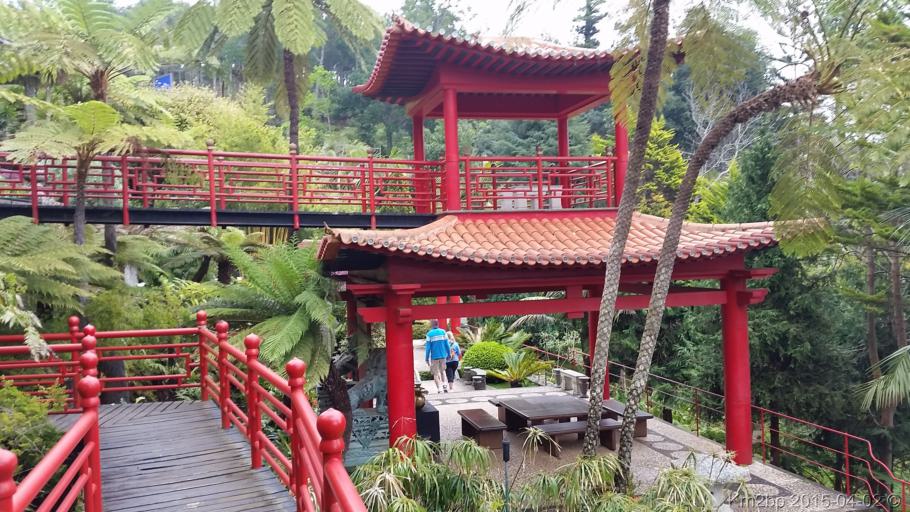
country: PT
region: Madeira
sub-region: Funchal
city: Nossa Senhora do Monte
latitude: 32.6733
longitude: -16.9028
